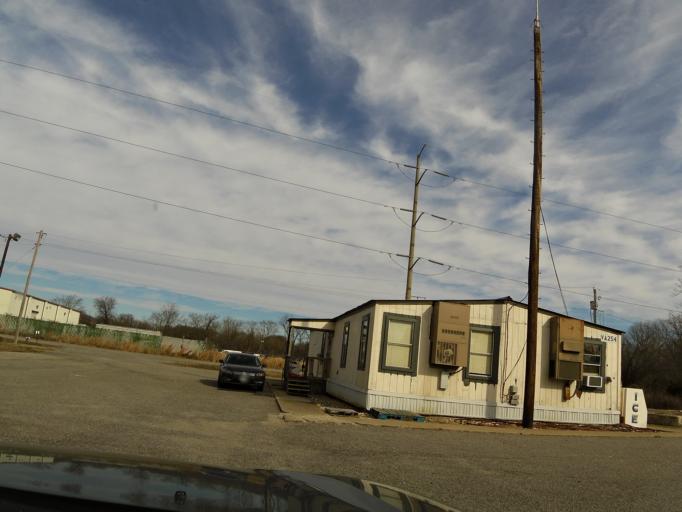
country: US
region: Virginia
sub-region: City of Hopewell
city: Hopewell
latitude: 37.2918
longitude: -77.2799
